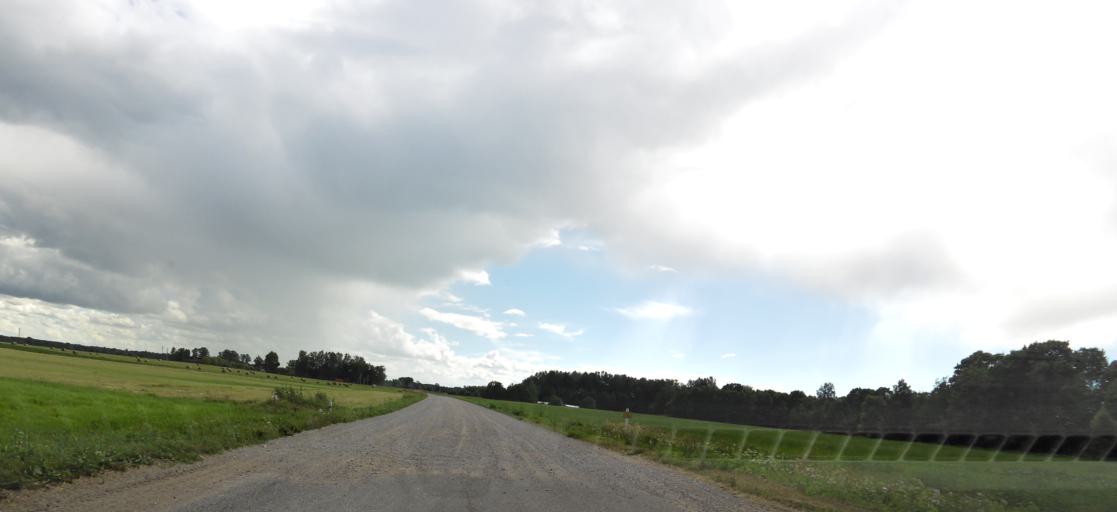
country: LT
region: Panevezys
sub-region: Birzai
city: Birzai
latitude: 56.3676
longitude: 24.6341
